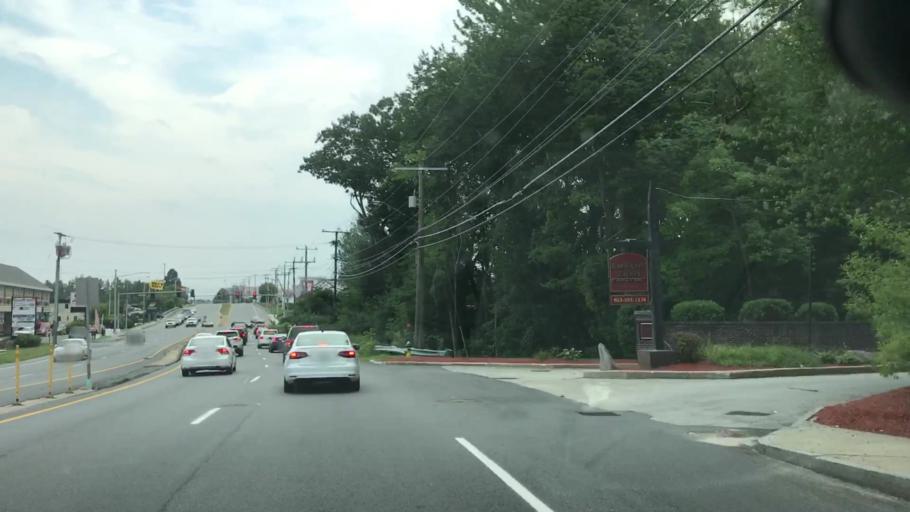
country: US
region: Massachusetts
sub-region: Middlesex County
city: Tyngsboro
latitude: 42.7157
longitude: -71.4429
